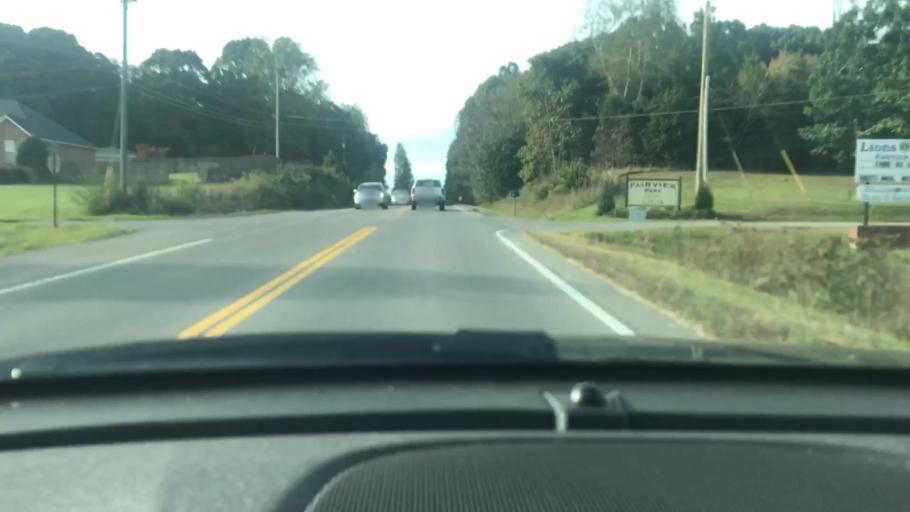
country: US
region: Tennessee
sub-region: Williamson County
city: Fairview
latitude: 35.9863
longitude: -87.1180
